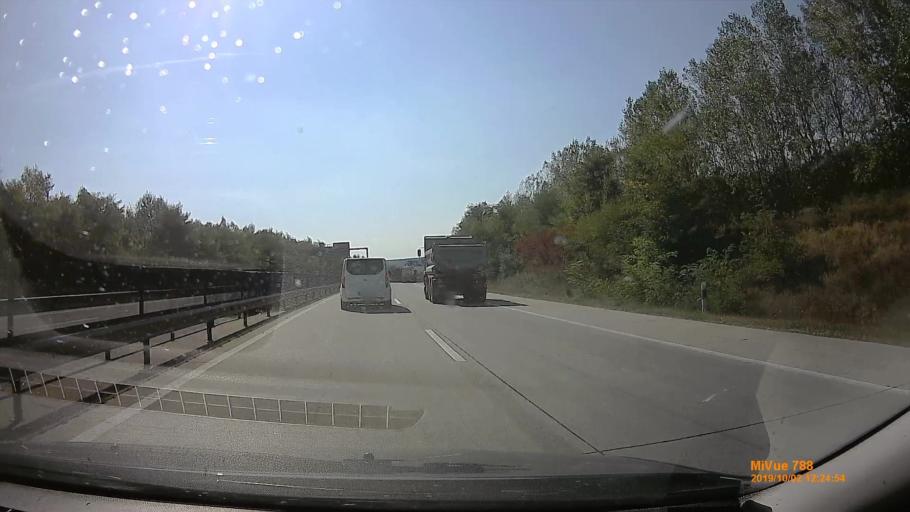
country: HU
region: Pest
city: Godollo
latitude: 47.5982
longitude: 19.3203
